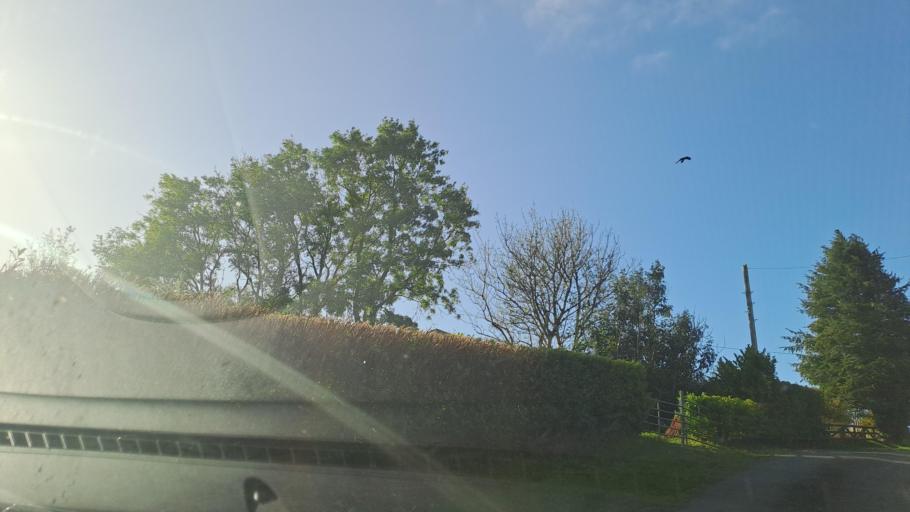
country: IE
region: Ulster
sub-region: An Cabhan
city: Kingscourt
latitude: 53.9624
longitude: -6.8622
